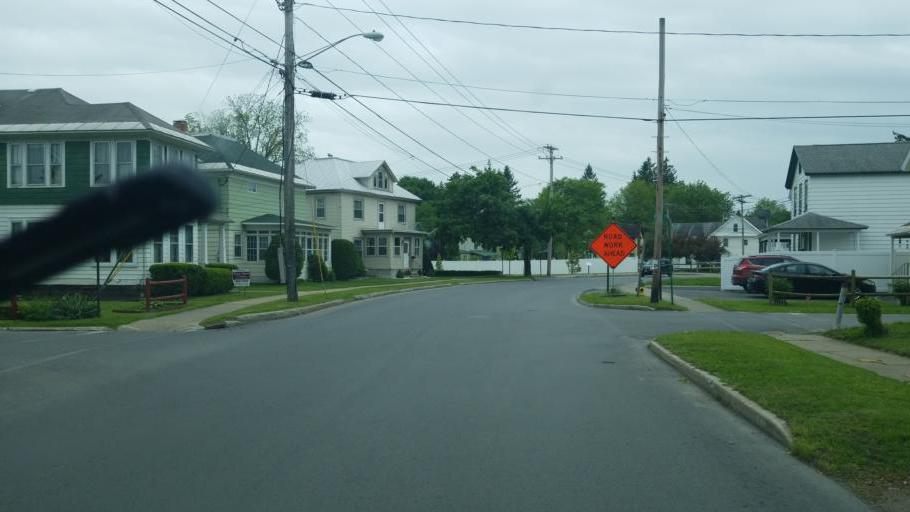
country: US
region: New York
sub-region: Herkimer County
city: Herkimer
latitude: 43.0320
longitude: -74.9888
